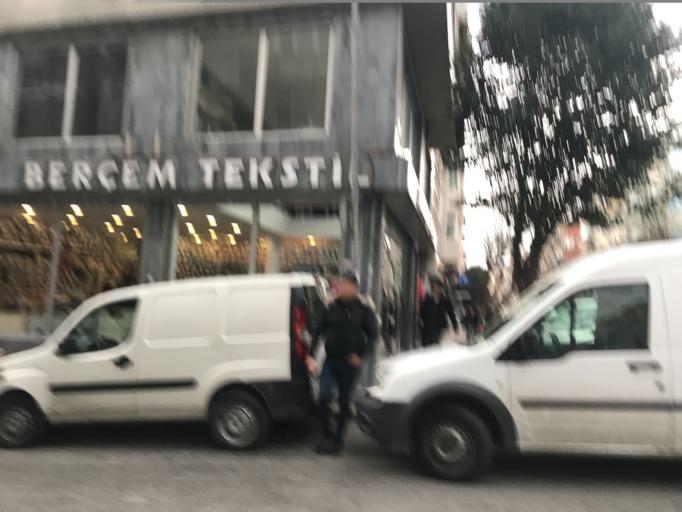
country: TR
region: Istanbul
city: Istanbul
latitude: 41.0192
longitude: 28.9457
